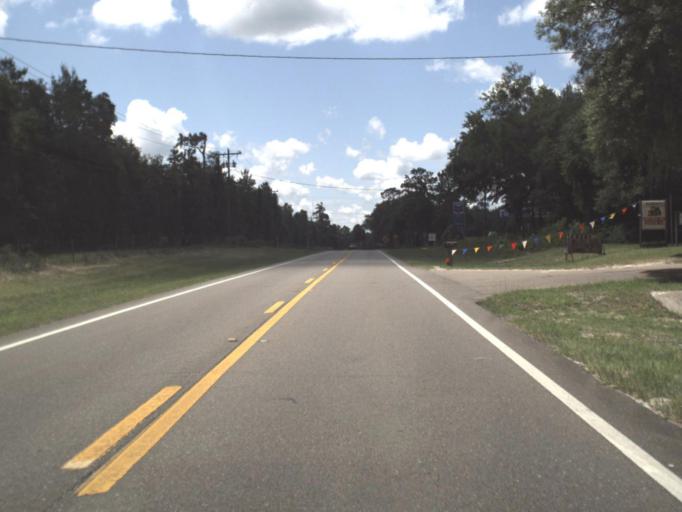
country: US
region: Florida
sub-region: Clay County
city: Keystone Heights
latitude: 29.7223
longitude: -82.0461
